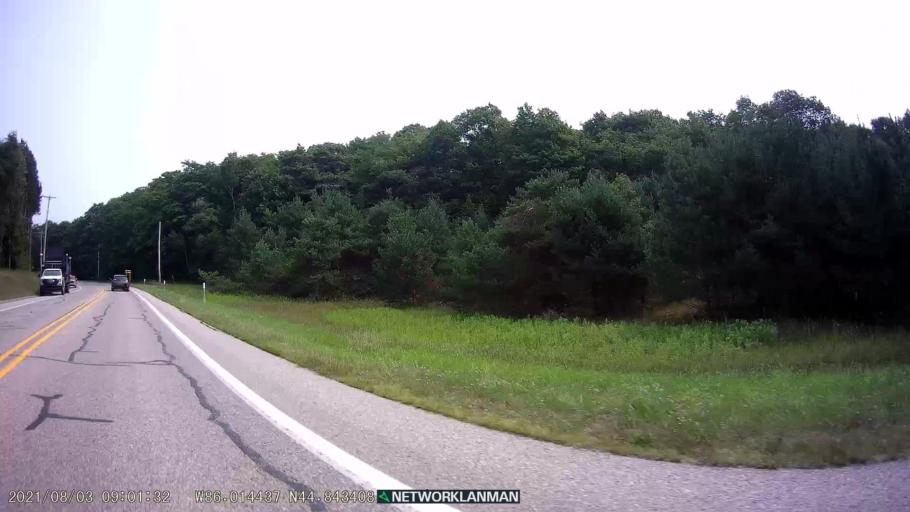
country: US
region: Michigan
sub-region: Benzie County
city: Beulah
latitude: 44.8434
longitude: -86.0147
